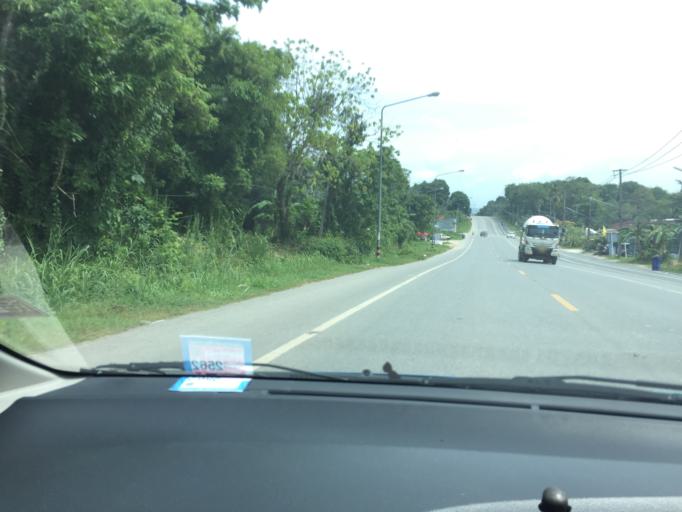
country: TH
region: Phuket
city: Mueang Phuket
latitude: 7.8381
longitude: 98.3928
